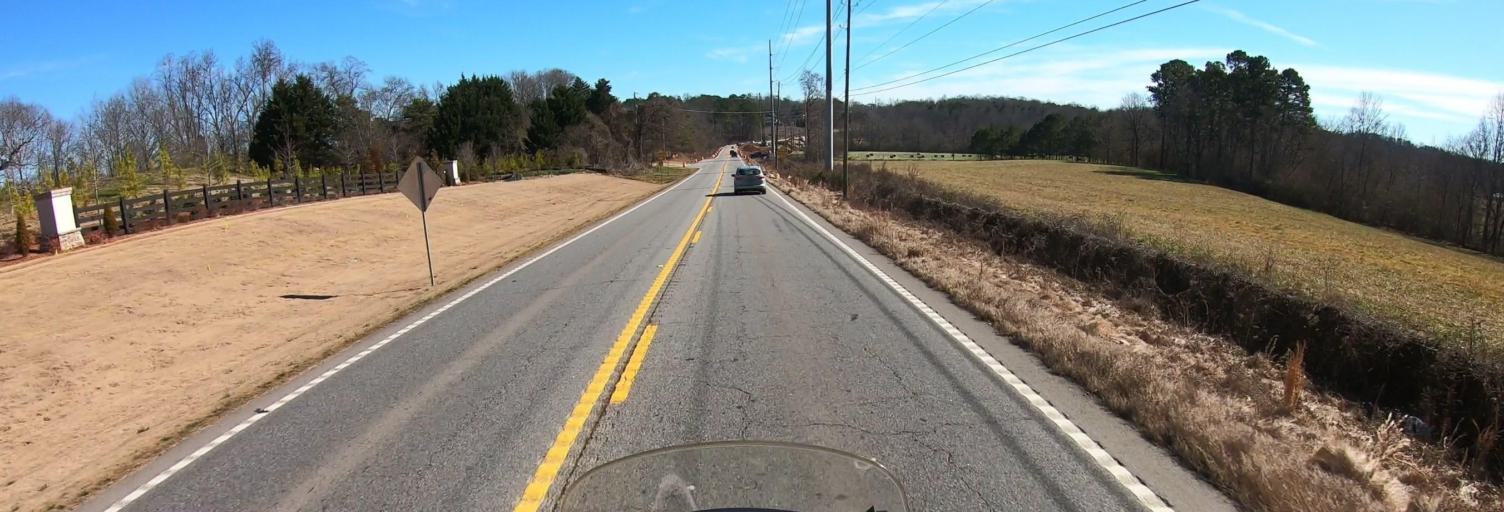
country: US
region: Georgia
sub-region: Forsyth County
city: Cumming
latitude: 34.2910
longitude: -84.1470
